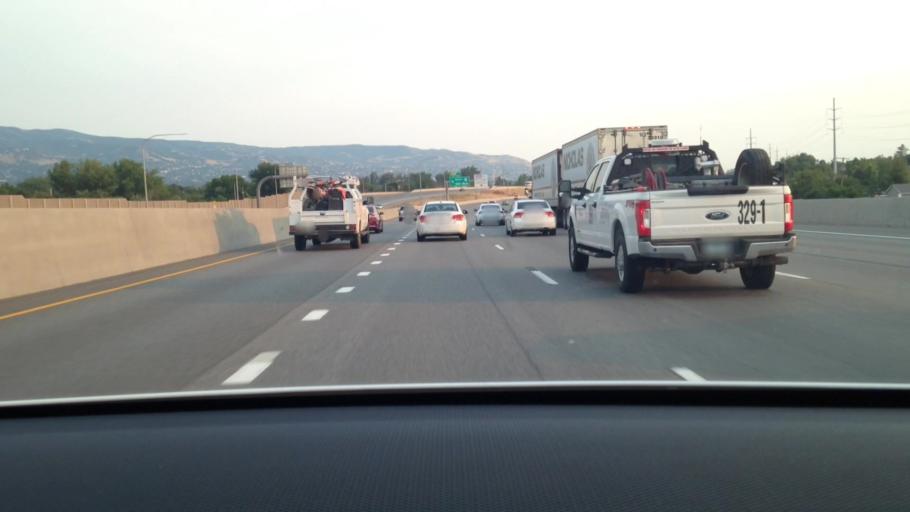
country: US
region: Utah
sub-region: Davis County
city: West Bountiful
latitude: 40.9059
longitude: -111.8915
